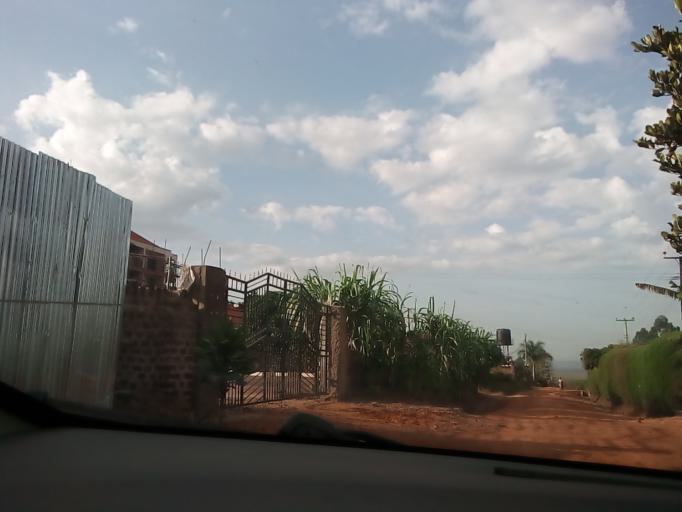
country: UG
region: Central Region
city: Masaka
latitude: -0.3477
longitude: 31.7248
